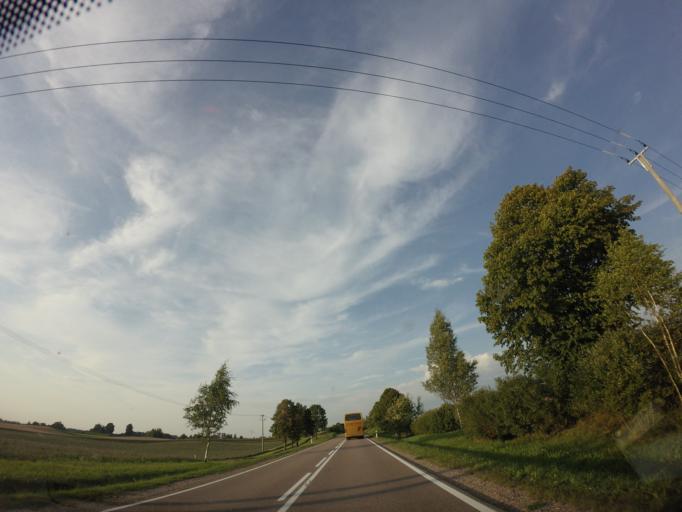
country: PL
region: Podlasie
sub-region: Powiat sejnenski
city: Sejny
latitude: 54.0842
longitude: 23.3803
